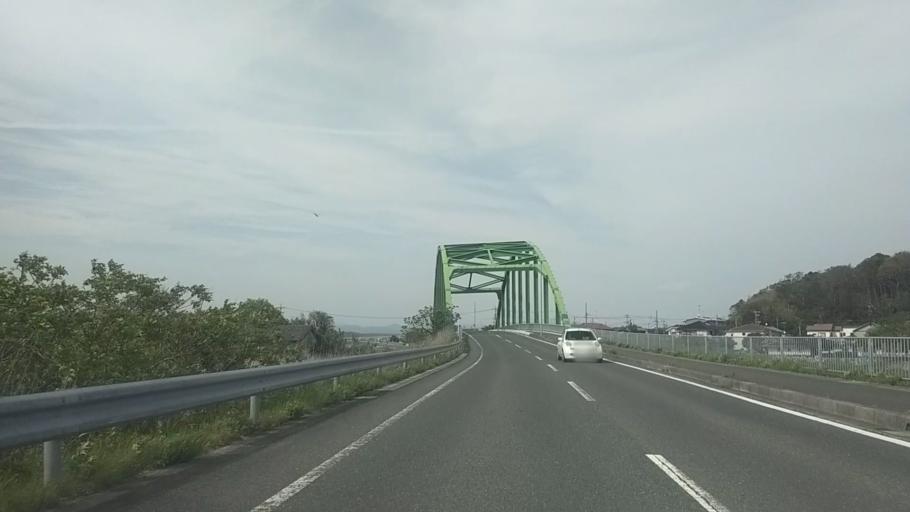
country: JP
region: Shizuoka
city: Kosai-shi
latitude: 34.7094
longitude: 137.6185
